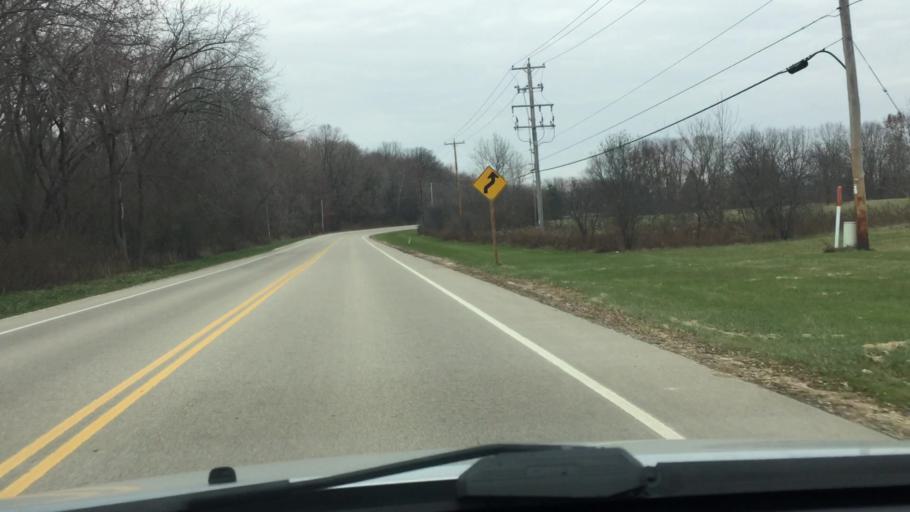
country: US
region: Wisconsin
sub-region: Ozaukee County
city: Thiensville
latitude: 43.2454
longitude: -87.9831
